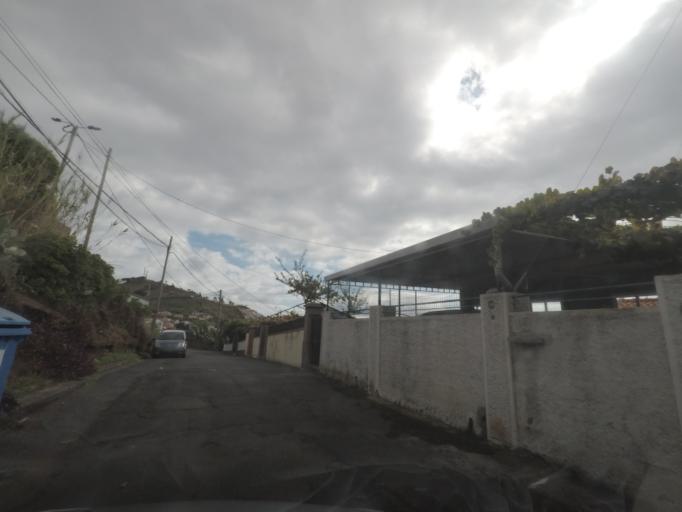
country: PT
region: Madeira
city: Camara de Lobos
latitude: 32.6475
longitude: -16.9462
